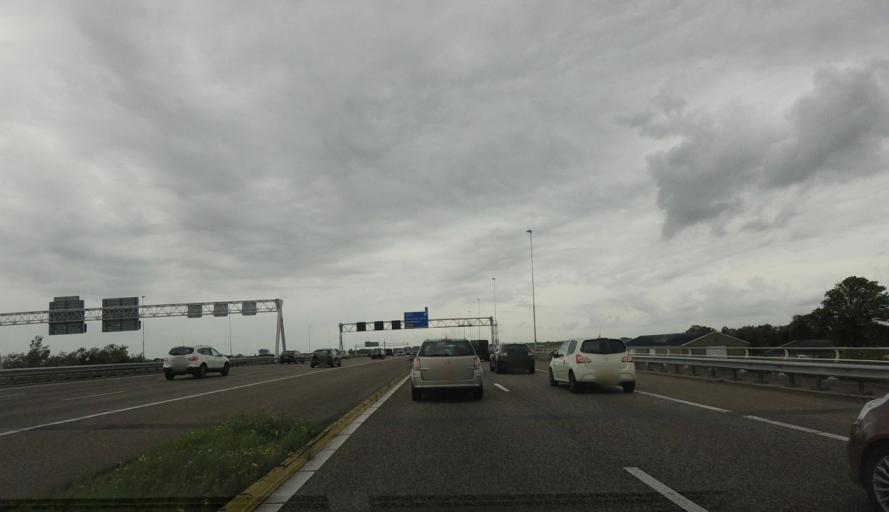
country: NL
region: North Holland
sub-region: Gemeente Haarlemmermeer
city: Hoofddorp
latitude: 52.3610
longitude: 4.7327
